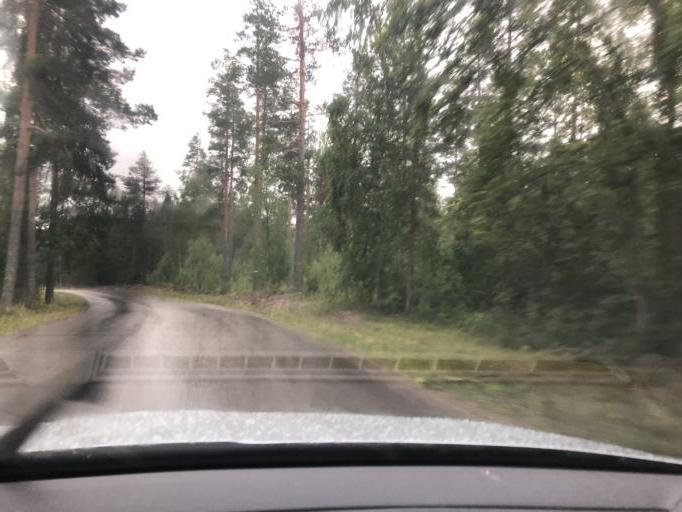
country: SE
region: Vaesternorrland
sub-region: Sundsvalls Kommun
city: Sundsvall
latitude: 62.4045
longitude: 17.3056
